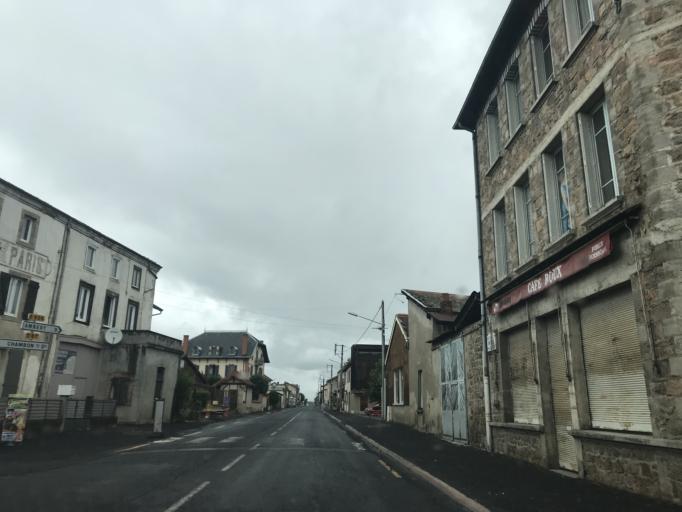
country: FR
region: Auvergne
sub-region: Departement du Puy-de-Dome
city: Marsac-en-Livradois
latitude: 45.4785
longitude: 3.7264
